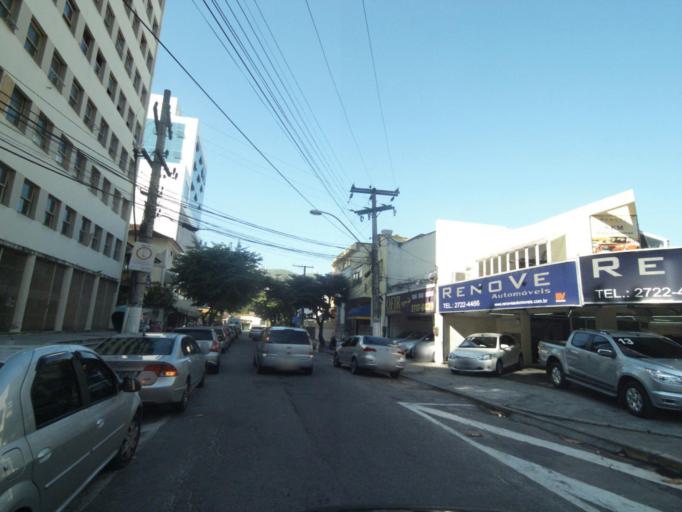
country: BR
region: Rio de Janeiro
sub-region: Niteroi
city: Niteroi
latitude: -22.8953
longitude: -43.1151
